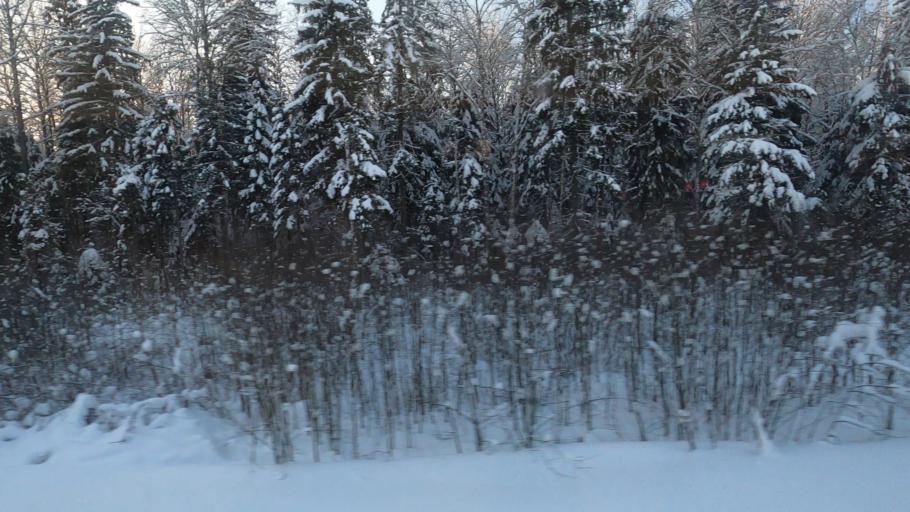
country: RU
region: Moskovskaya
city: Novo-Nikol'skoye
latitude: 56.6047
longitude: 37.5678
